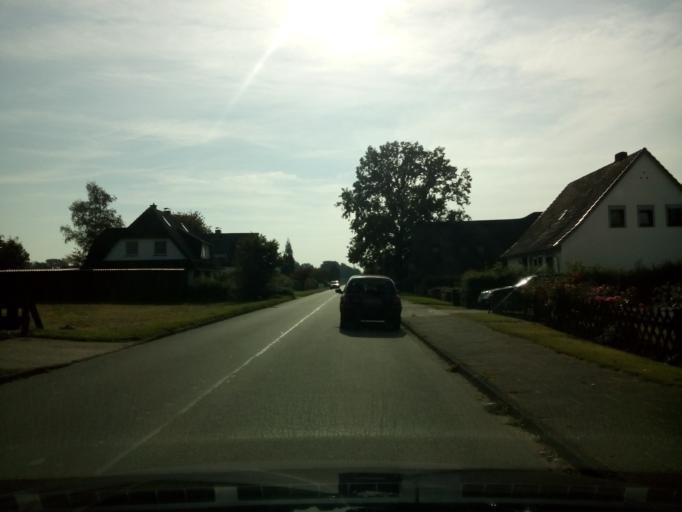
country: DE
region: Lower Saxony
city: Osterholz-Scharmbeck
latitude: 53.2348
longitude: 8.7631
